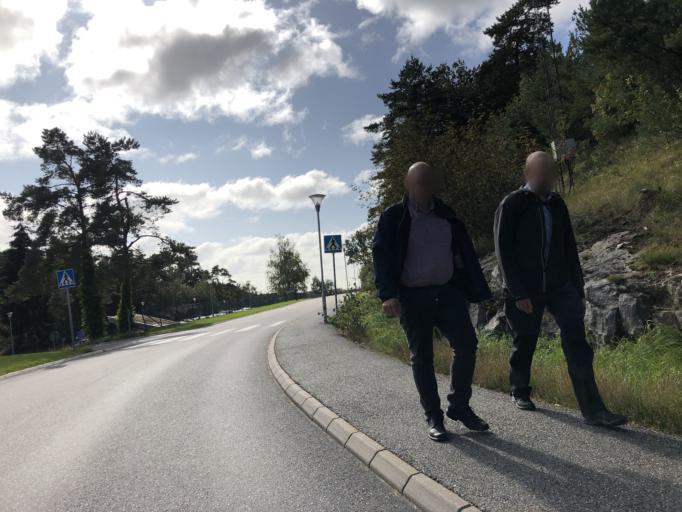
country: SE
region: Vaestra Goetaland
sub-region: Goteborg
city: Majorna
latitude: 57.7287
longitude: 11.8547
